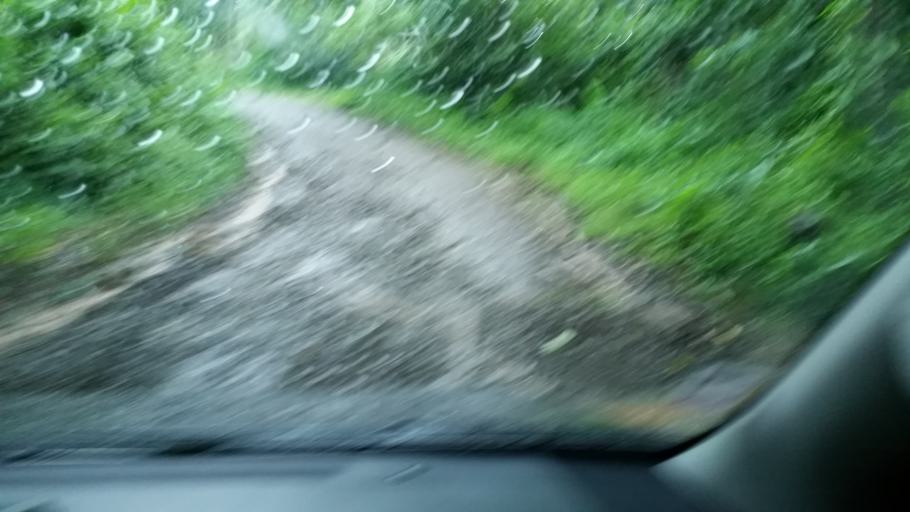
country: NI
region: Atlantico Norte (RAAN)
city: Waslala
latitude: 13.1629
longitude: -85.4186
